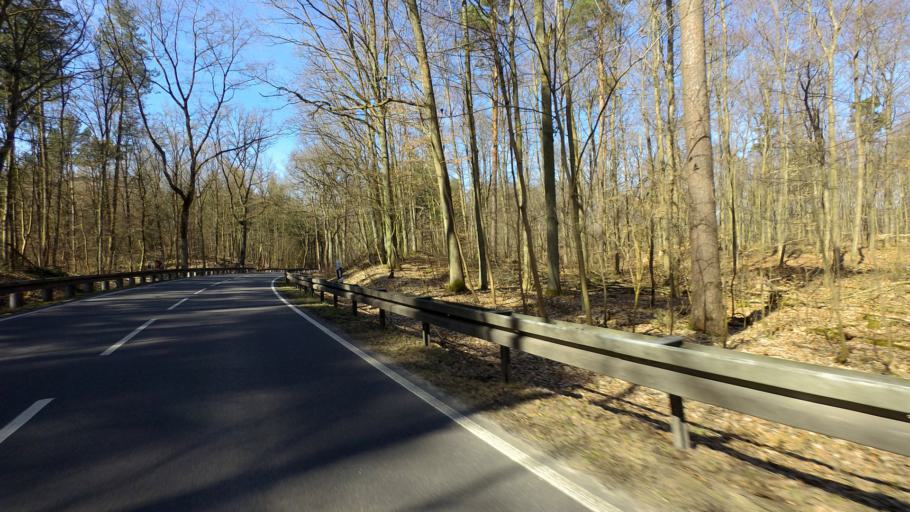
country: DE
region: Brandenburg
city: Waldsieversdorf
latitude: 52.5356
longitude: 14.0616
